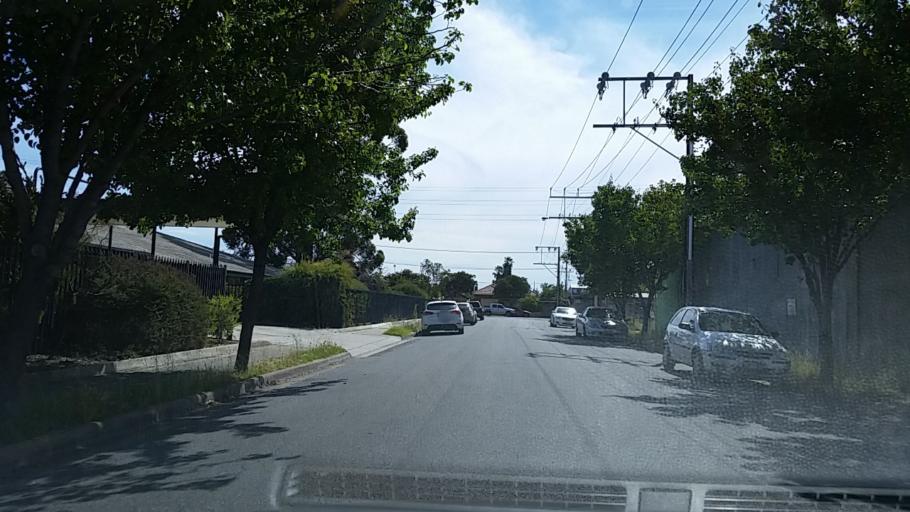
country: AU
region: South Australia
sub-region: Charles Sturt
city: Royal Park
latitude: -34.8724
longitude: 138.5135
